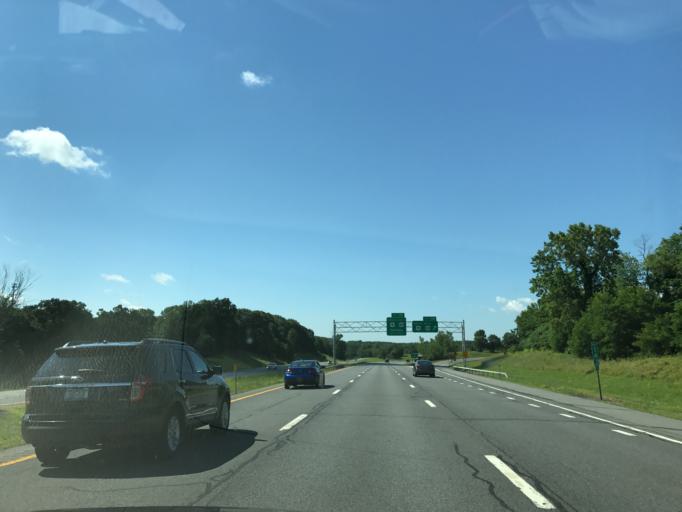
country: US
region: New York
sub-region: Rensselaer County
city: East Greenbush
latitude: 42.5646
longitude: -73.6789
